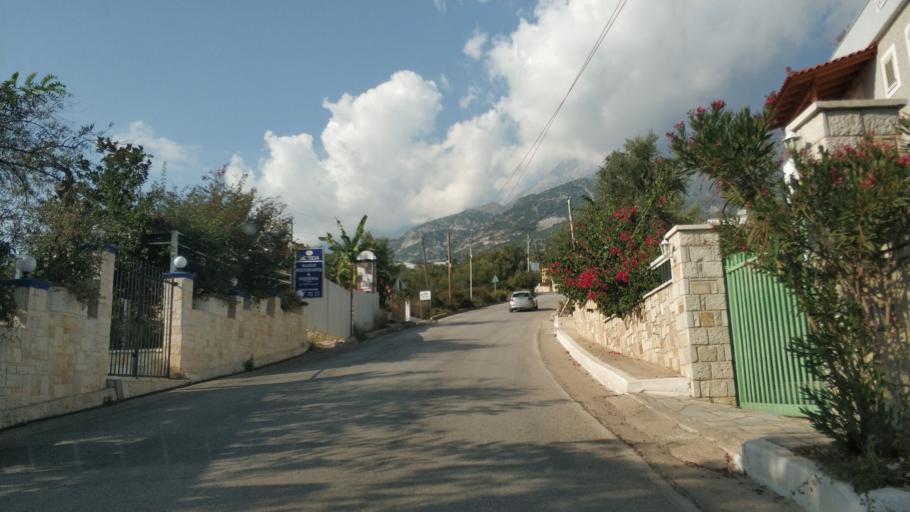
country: AL
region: Vlore
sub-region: Rrethi i Vlores
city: Vranisht
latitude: 40.1468
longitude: 19.6343
